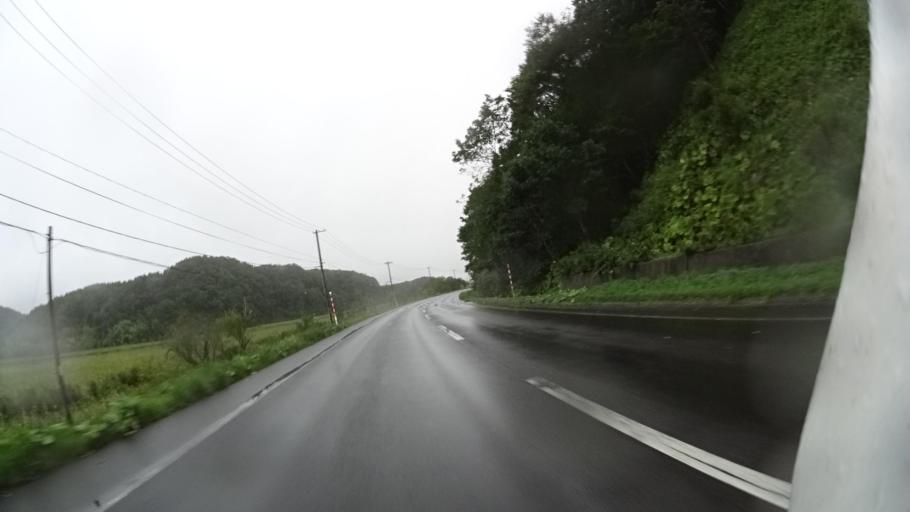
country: JP
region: Hokkaido
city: Kushiro
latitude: 43.0796
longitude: 144.8421
